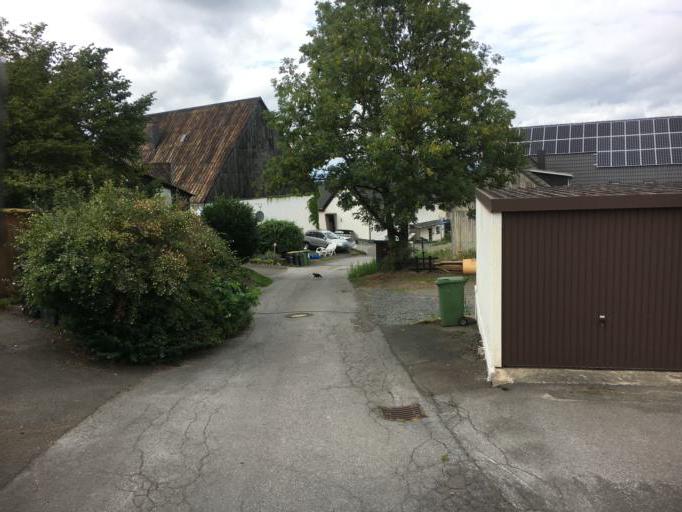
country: DE
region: North Rhine-Westphalia
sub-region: Regierungsbezirk Arnsberg
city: Herscheid
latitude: 51.2109
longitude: 7.7746
